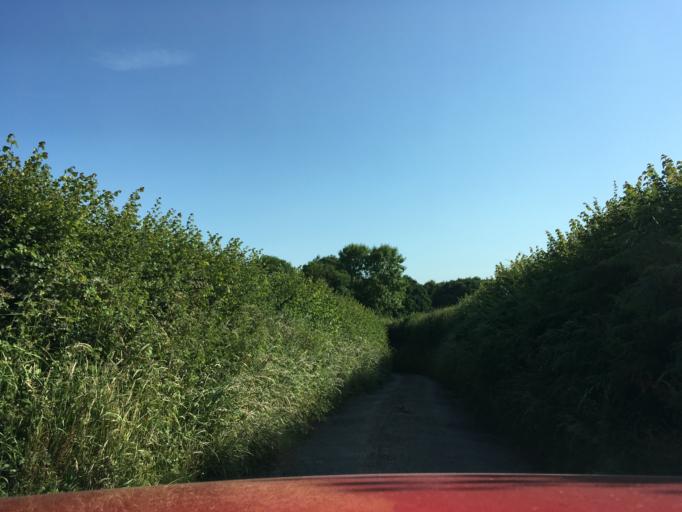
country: GB
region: England
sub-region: Gloucestershire
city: Berkeley
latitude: 51.7549
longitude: -2.4642
